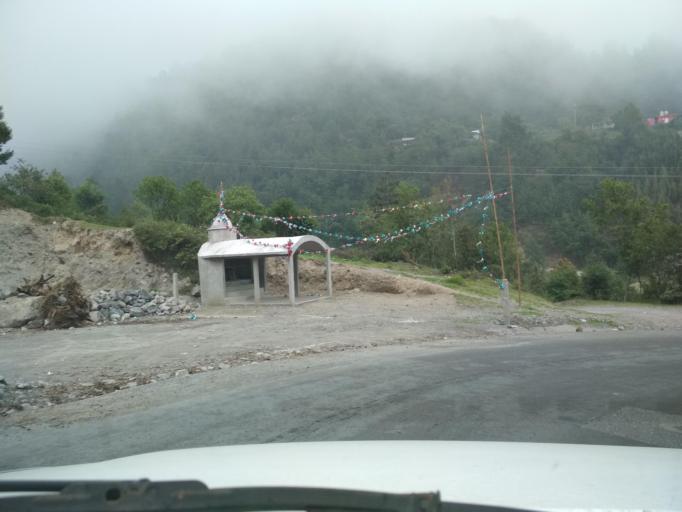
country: MX
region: Veracruz
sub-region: Mariano Escobedo
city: San Isidro el Berro
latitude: 18.9485
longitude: -97.2005
